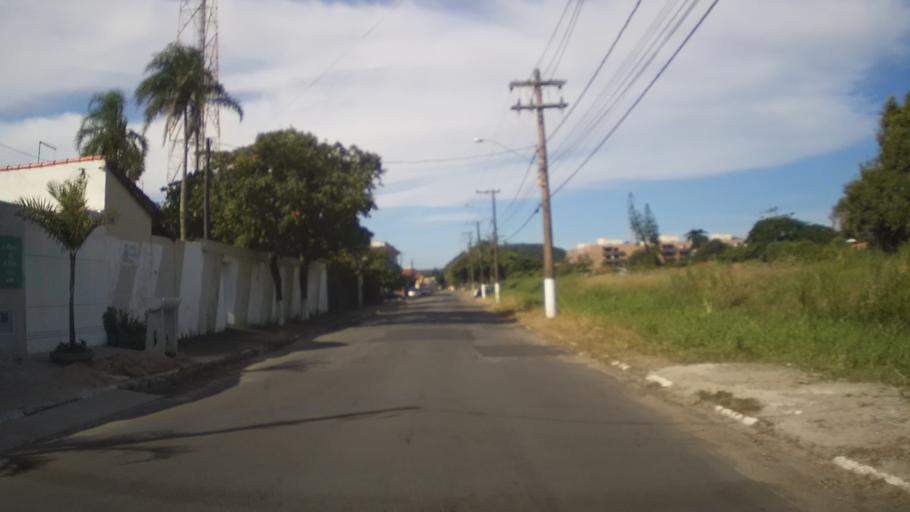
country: BR
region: Sao Paulo
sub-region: Itanhaem
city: Itanhaem
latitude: -24.1965
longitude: -46.8161
